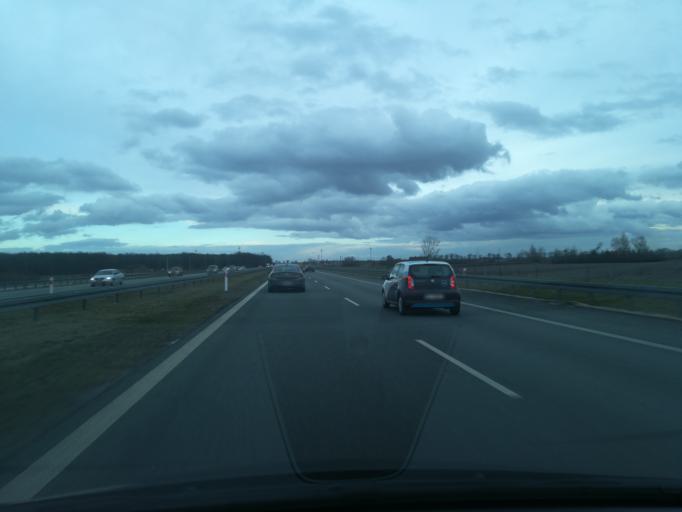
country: PL
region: Lodz Voivodeship
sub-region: Powiat kutnowski
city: Strzelce
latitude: 52.2630
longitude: 19.4320
